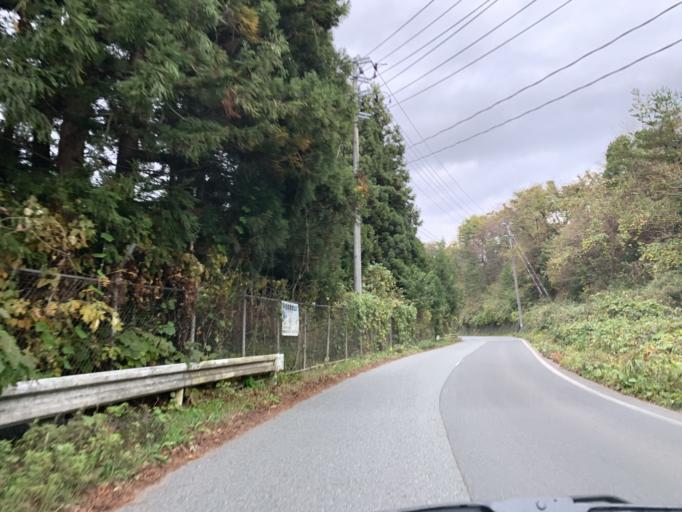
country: JP
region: Iwate
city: Mizusawa
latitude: 39.0501
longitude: 141.1125
